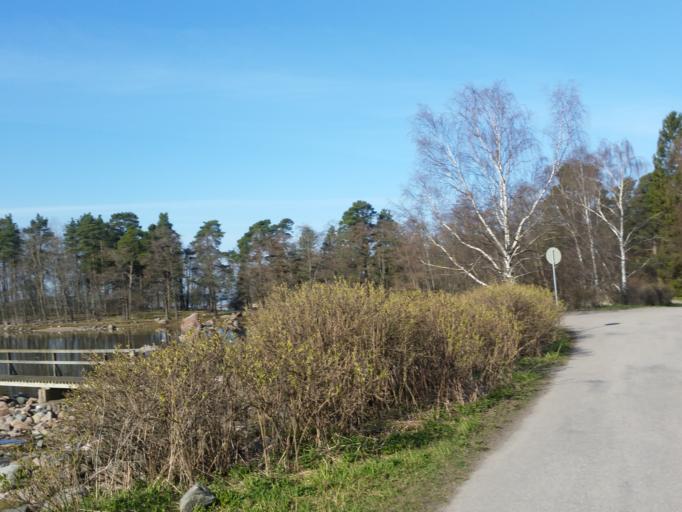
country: FI
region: Uusimaa
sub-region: Helsinki
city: Teekkarikylae
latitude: 60.1542
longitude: 24.8667
